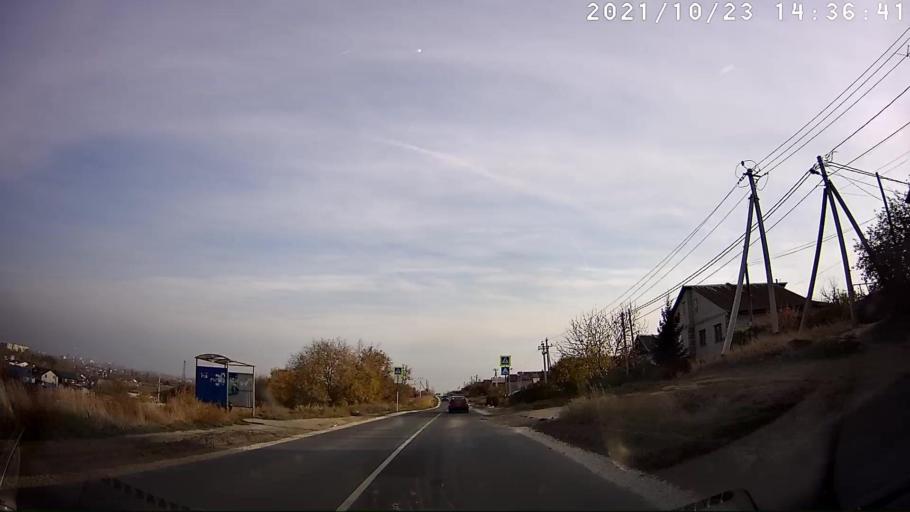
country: RU
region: Volgograd
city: Krasnoslobodsk
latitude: 48.5016
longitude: 44.5429
